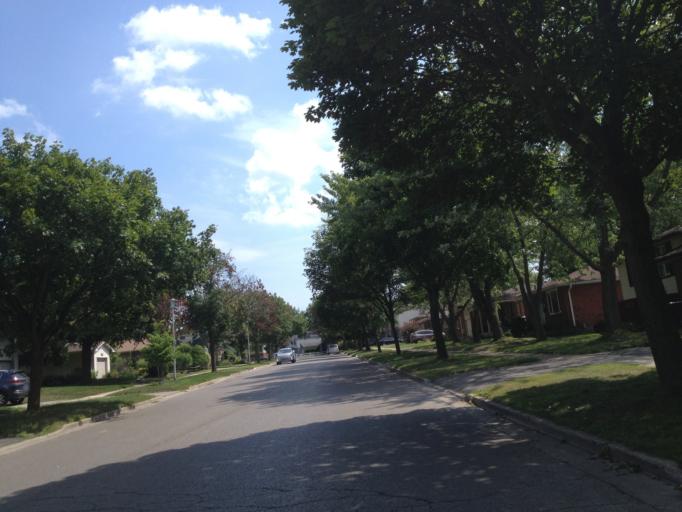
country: CA
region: Ontario
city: London
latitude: 43.0061
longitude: -81.3181
